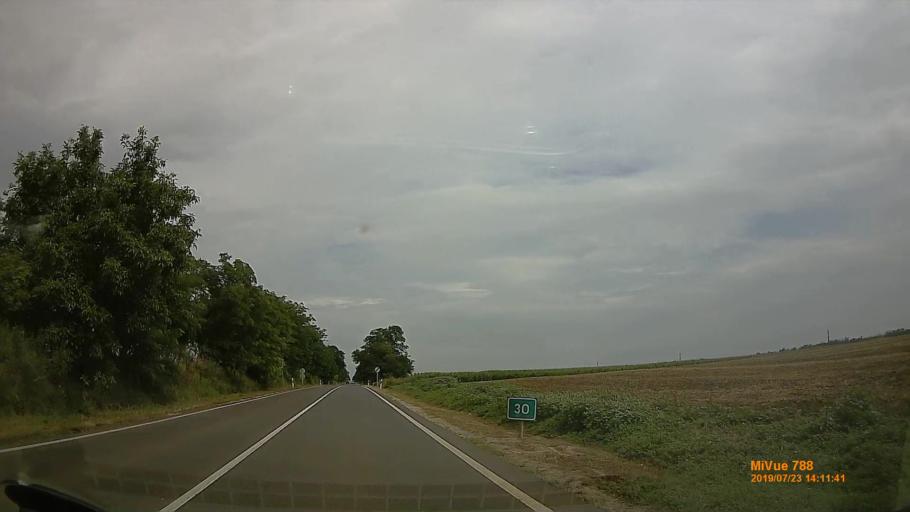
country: HU
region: Szabolcs-Szatmar-Bereg
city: Tiszalok
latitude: 47.9597
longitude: 21.4387
